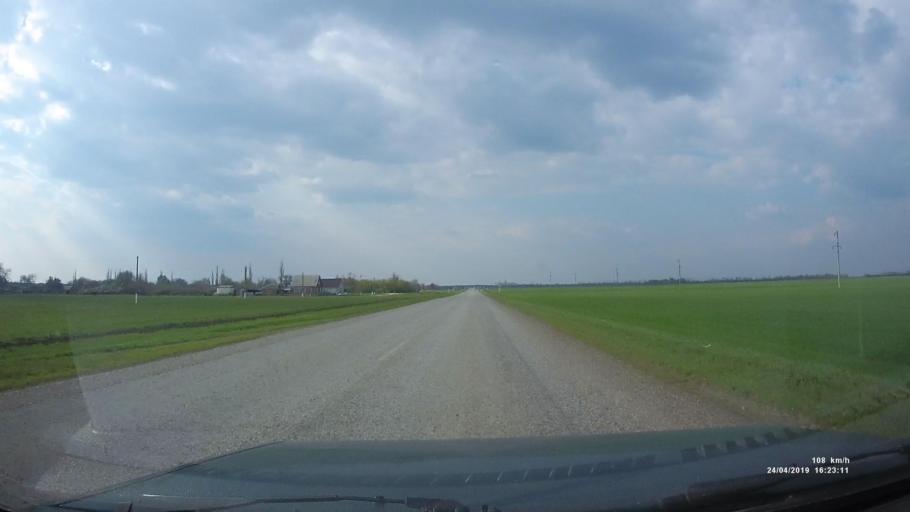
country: RU
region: Rostov
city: Orlovskiy
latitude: 46.8308
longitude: 42.0510
